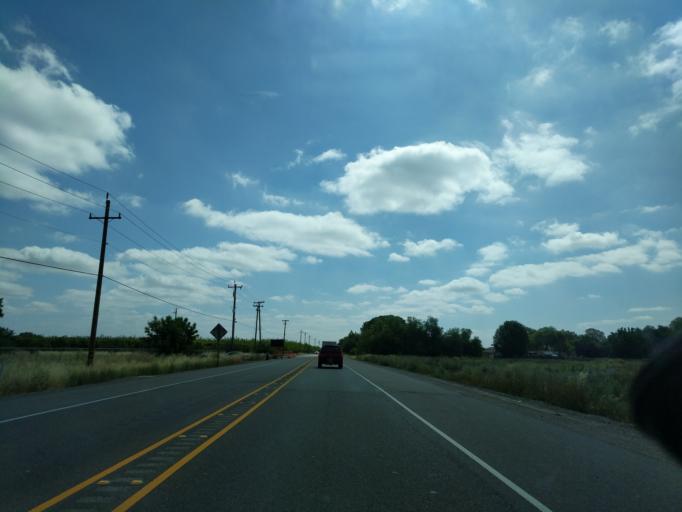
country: US
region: California
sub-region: Contra Costa County
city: Brentwood
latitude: 37.8963
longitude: -121.6923
